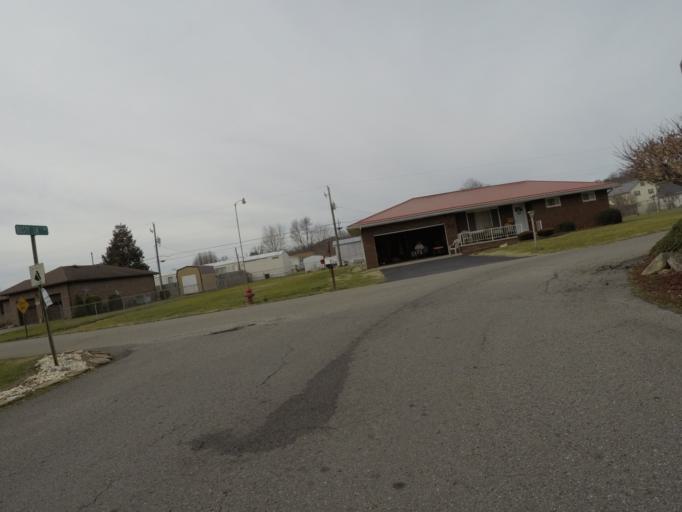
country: US
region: West Virginia
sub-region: Cabell County
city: Pea Ridge
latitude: 38.4531
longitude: -82.3461
